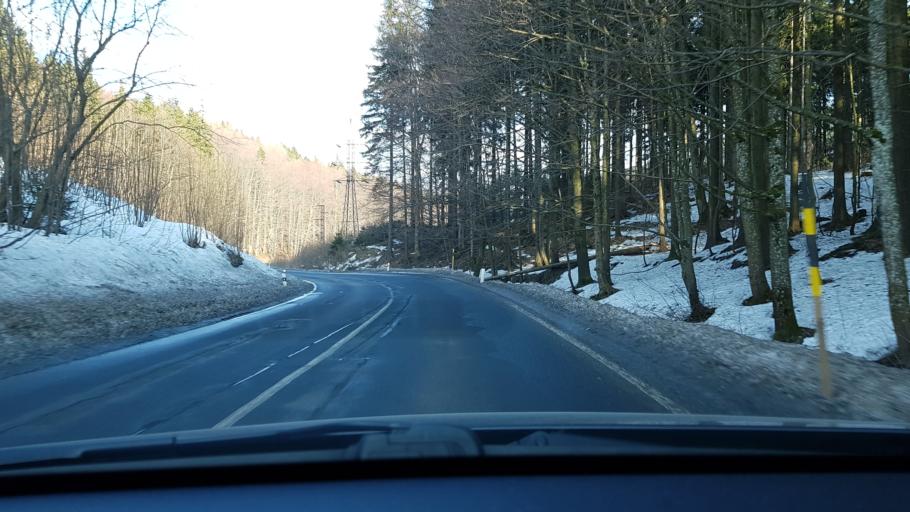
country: CZ
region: Olomoucky
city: Vapenna
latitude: 50.2047
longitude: 17.0753
